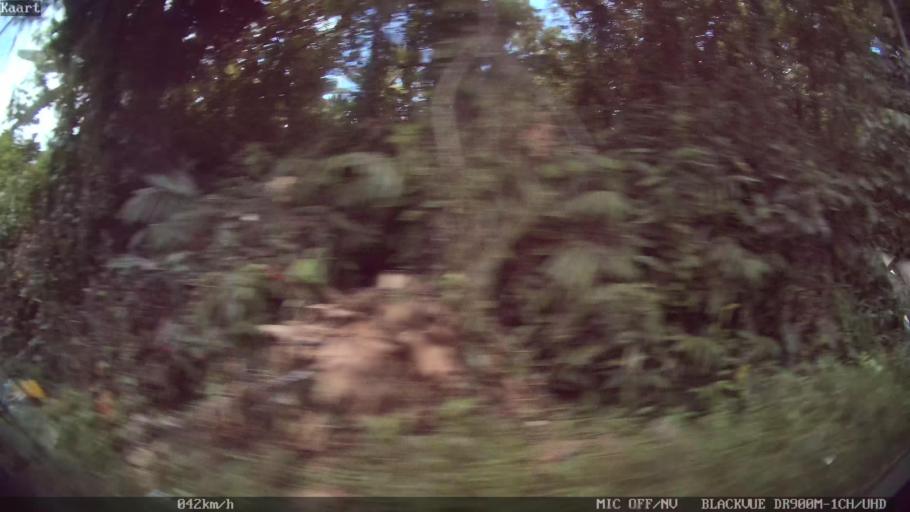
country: ID
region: Bali
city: Banjar Mulung
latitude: -8.5114
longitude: 115.3191
